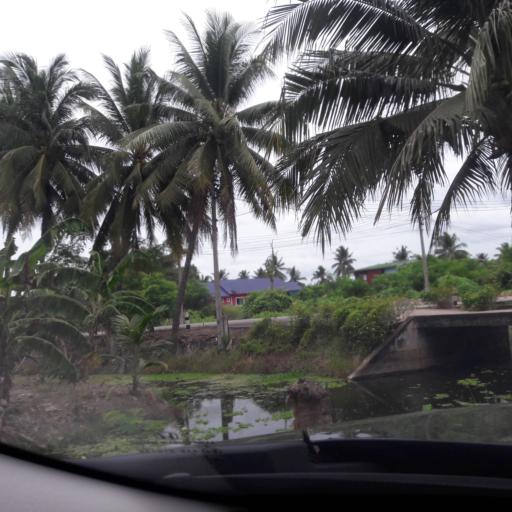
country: TH
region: Ratchaburi
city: Damnoen Saduak
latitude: 13.5707
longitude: 99.9490
